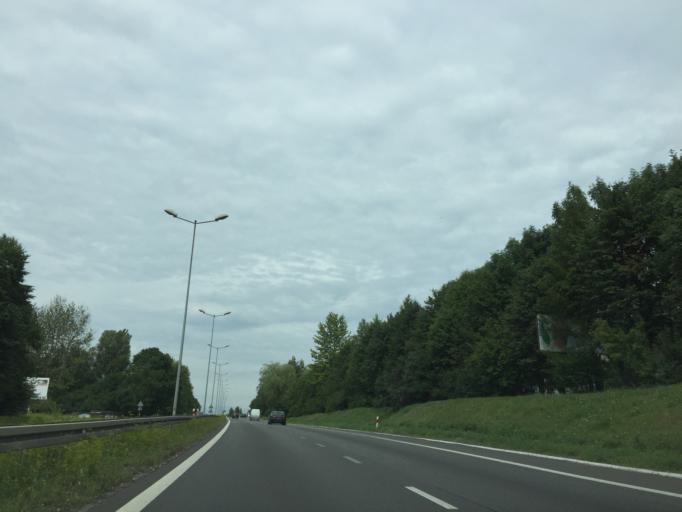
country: PL
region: Lesser Poland Voivodeship
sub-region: Powiat olkuski
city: Olkusz
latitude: 50.2754
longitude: 19.5823
